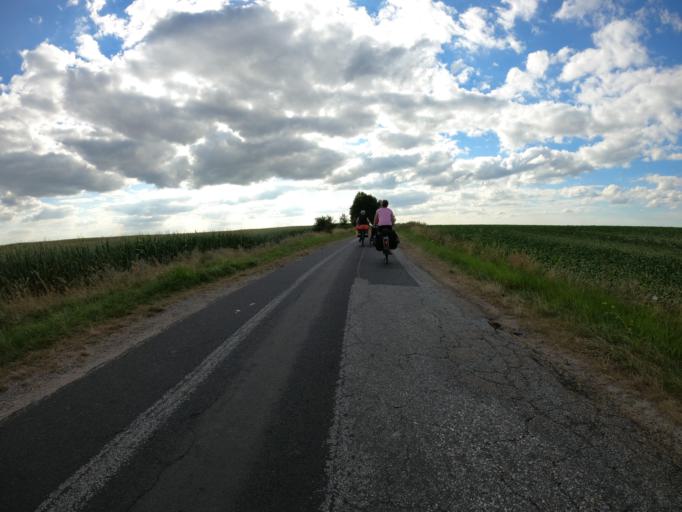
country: PL
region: West Pomeranian Voivodeship
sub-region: Powiat swidwinski
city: Swidwin
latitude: 53.7585
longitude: 15.6626
